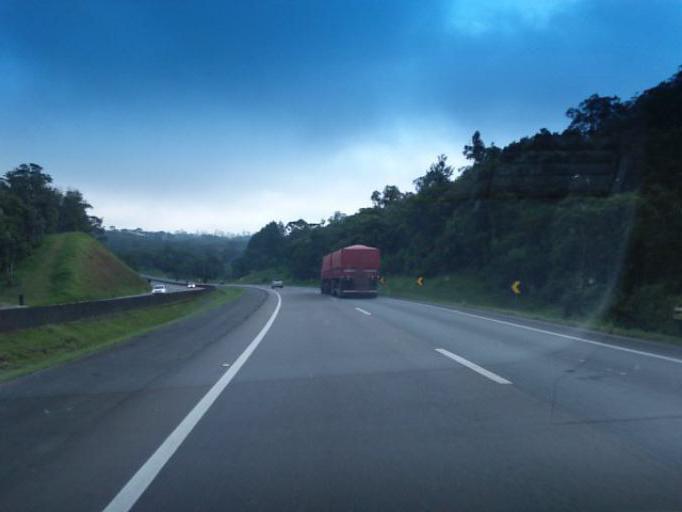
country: BR
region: Parana
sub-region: Sao Jose Dos Pinhais
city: Sao Jose dos Pinhais
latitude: -25.8021
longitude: -49.1344
